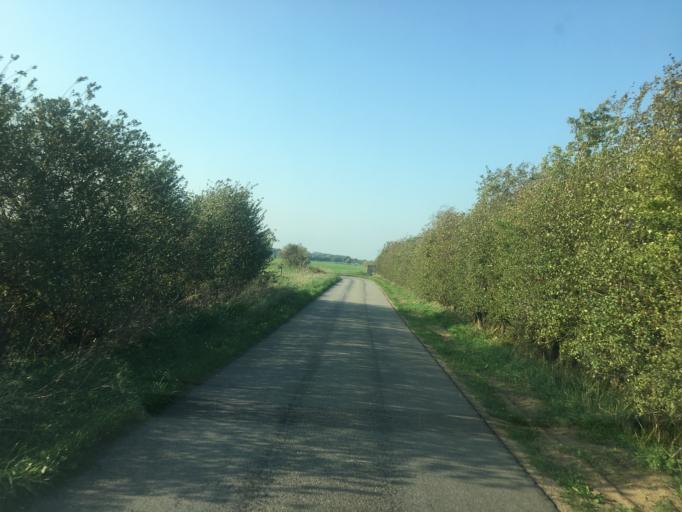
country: DE
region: Schleswig-Holstein
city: Ladelund
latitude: 54.9228
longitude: 9.0351
